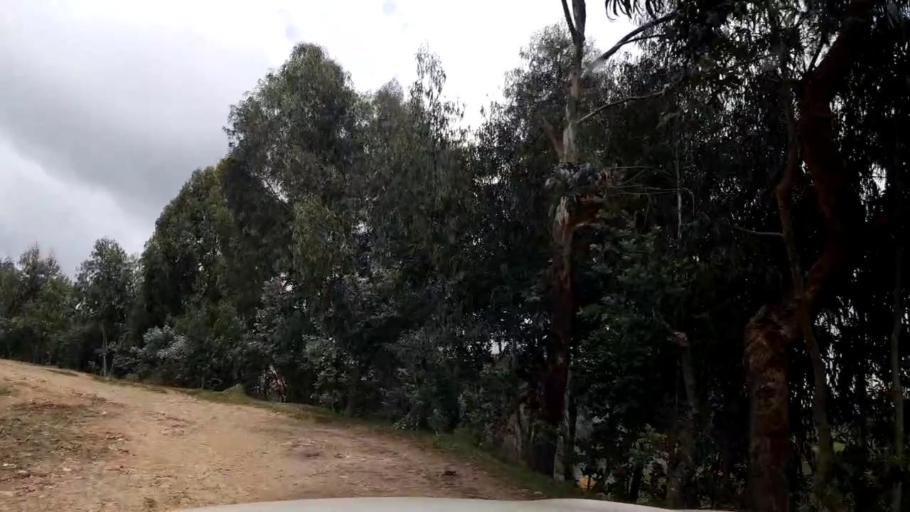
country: RW
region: Western Province
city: Kibuye
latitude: -1.8963
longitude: 29.4558
